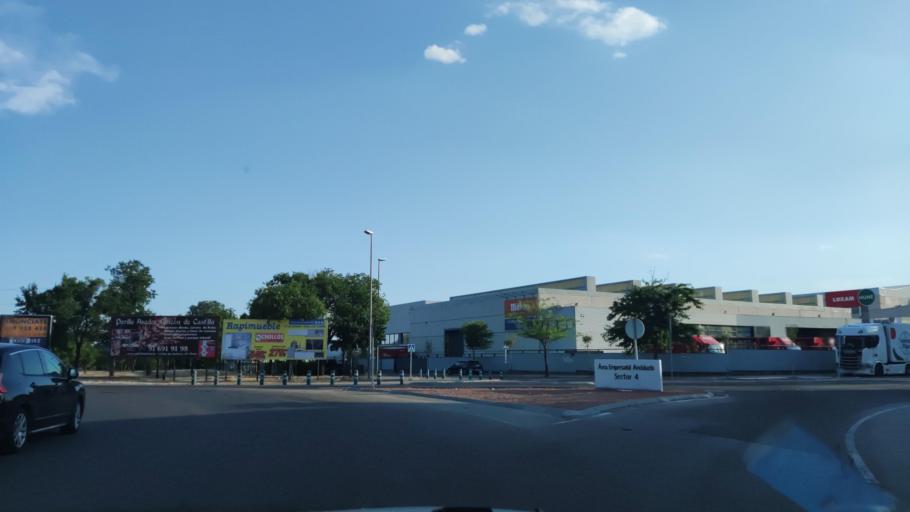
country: ES
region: Madrid
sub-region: Provincia de Madrid
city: Pinto
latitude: 40.2710
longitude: -3.7001
